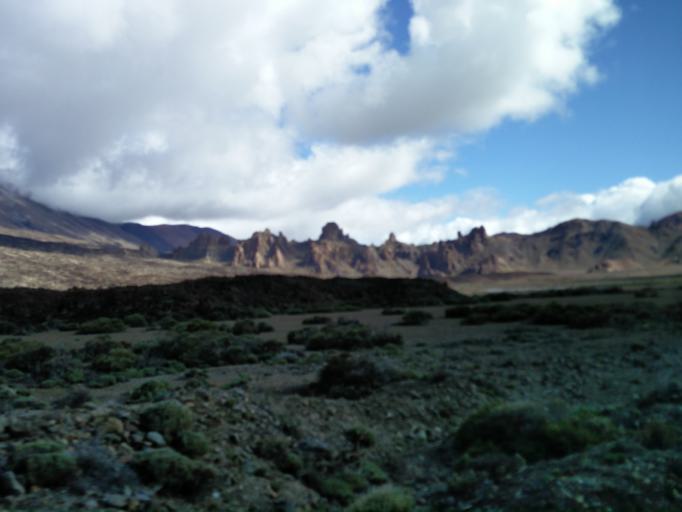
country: ES
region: Canary Islands
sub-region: Provincia de Santa Cruz de Tenerife
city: Vilaflor
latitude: 28.2109
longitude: -16.6527
